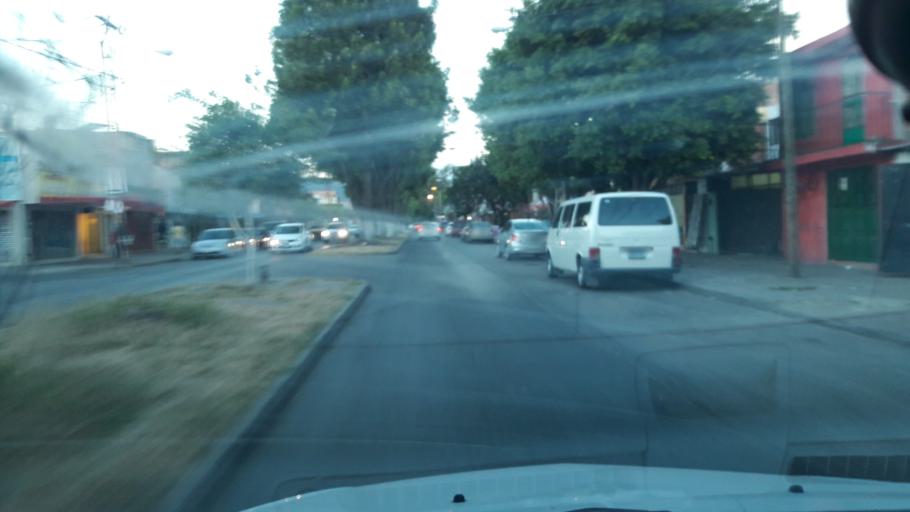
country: MX
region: Guanajuato
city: Leon
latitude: 21.1656
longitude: -101.6689
